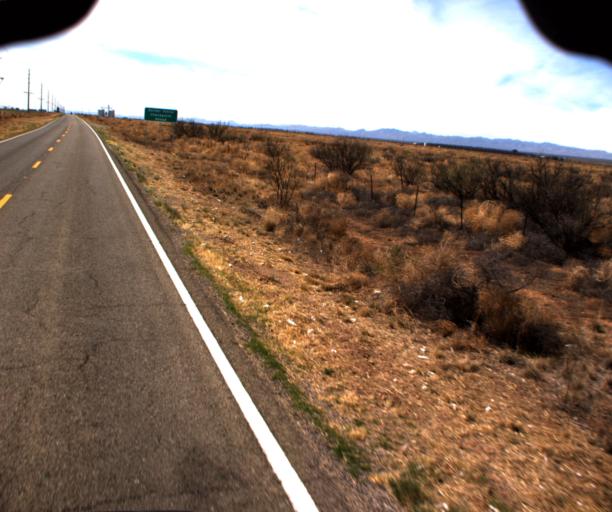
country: US
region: Arizona
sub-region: Cochise County
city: Tombstone
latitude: 31.7746
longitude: -109.6910
